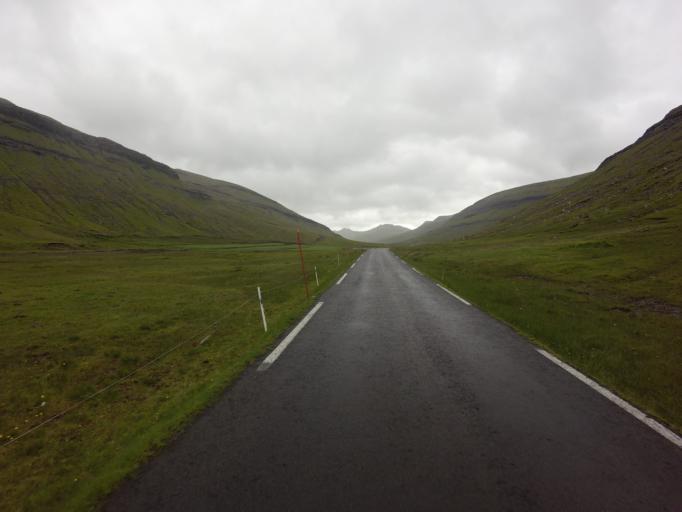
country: FO
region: Streymoy
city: Vestmanna
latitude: 62.2312
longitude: -7.1378
